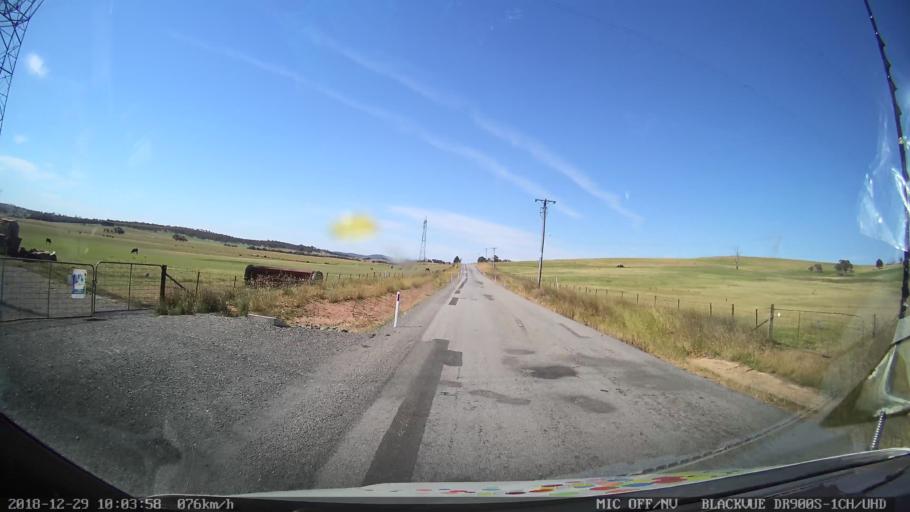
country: AU
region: New South Wales
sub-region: Goulburn Mulwaree
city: Goulburn
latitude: -34.8167
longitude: 149.4564
